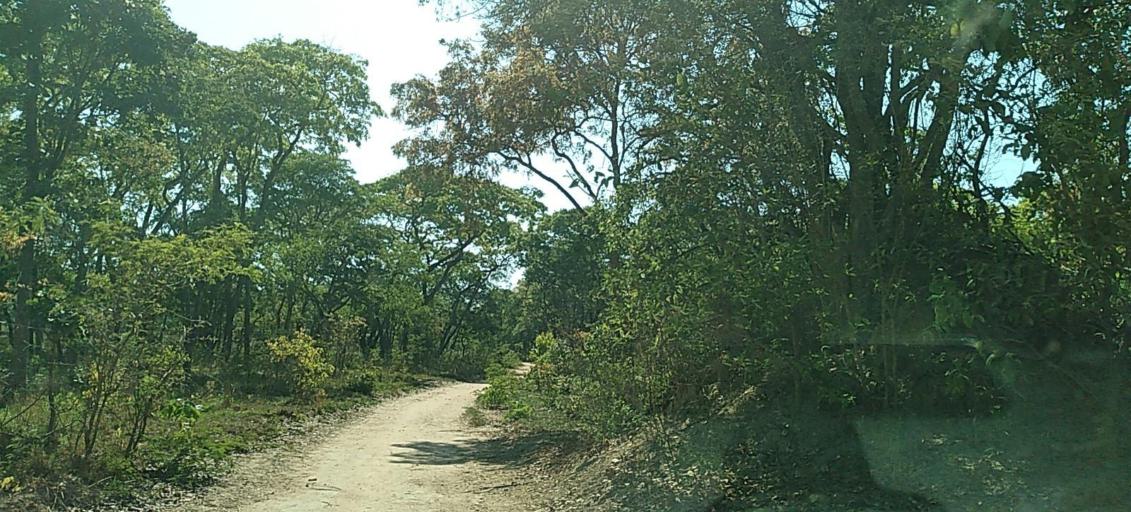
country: ZM
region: Central
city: Mkushi
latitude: -13.4703
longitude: 28.9744
